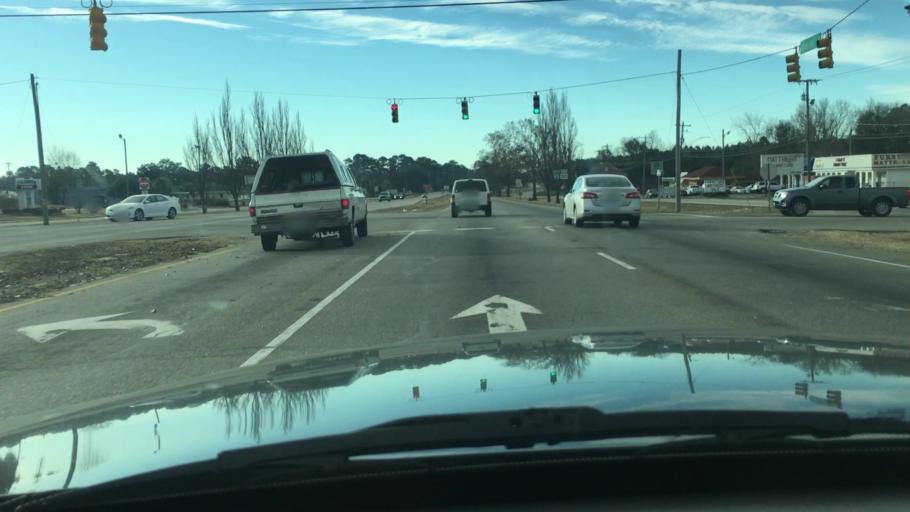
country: US
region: North Carolina
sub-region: Cumberland County
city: Fayetteville
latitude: 35.0134
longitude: -78.8972
